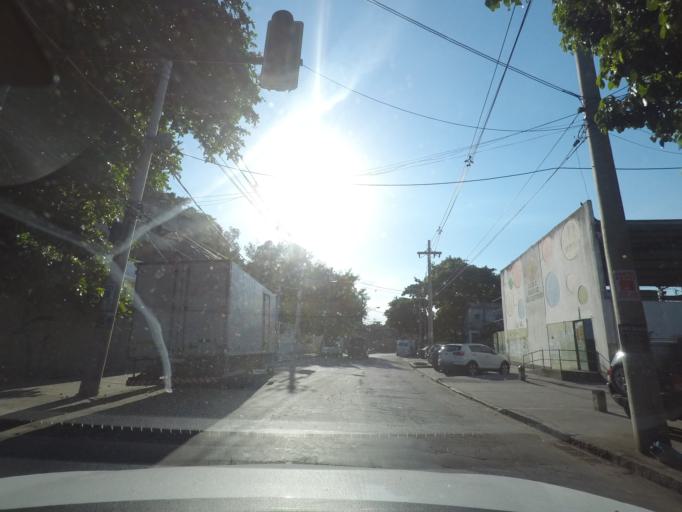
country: BR
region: Rio de Janeiro
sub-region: Rio De Janeiro
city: Rio de Janeiro
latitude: -22.8901
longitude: -43.2300
